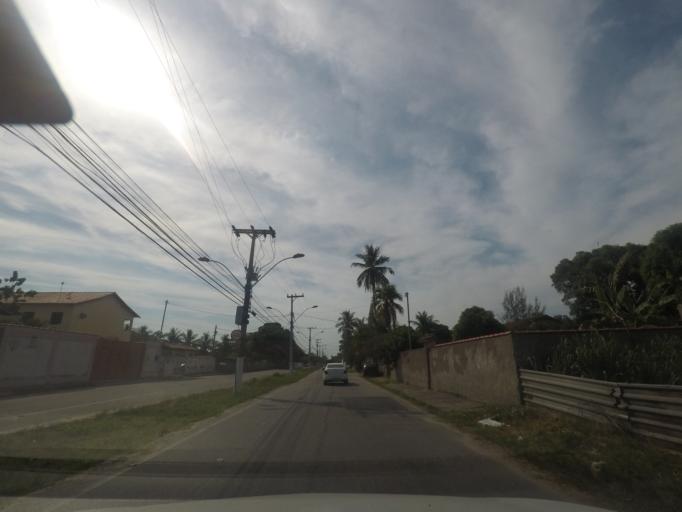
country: BR
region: Rio de Janeiro
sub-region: Marica
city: Marica
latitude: -22.9360
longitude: -42.8996
